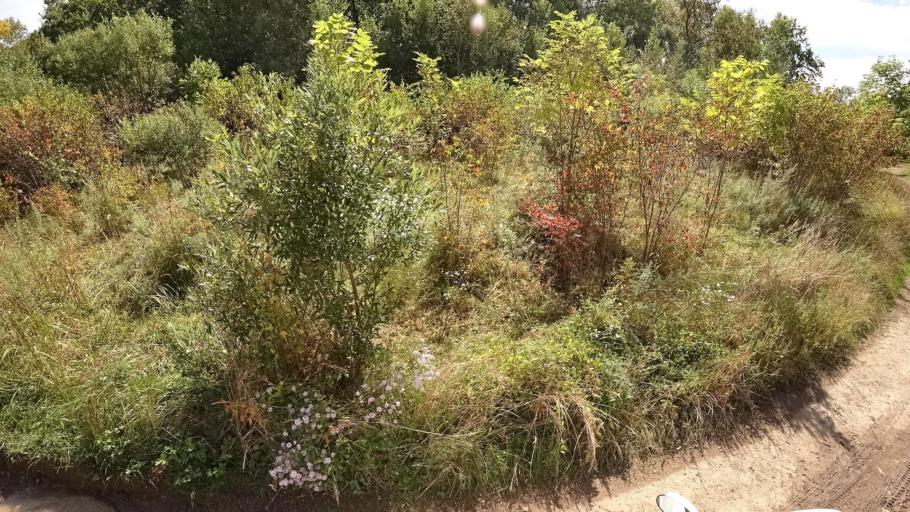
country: RU
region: Primorskiy
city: Kirovskiy
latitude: 44.7580
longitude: 133.6192
